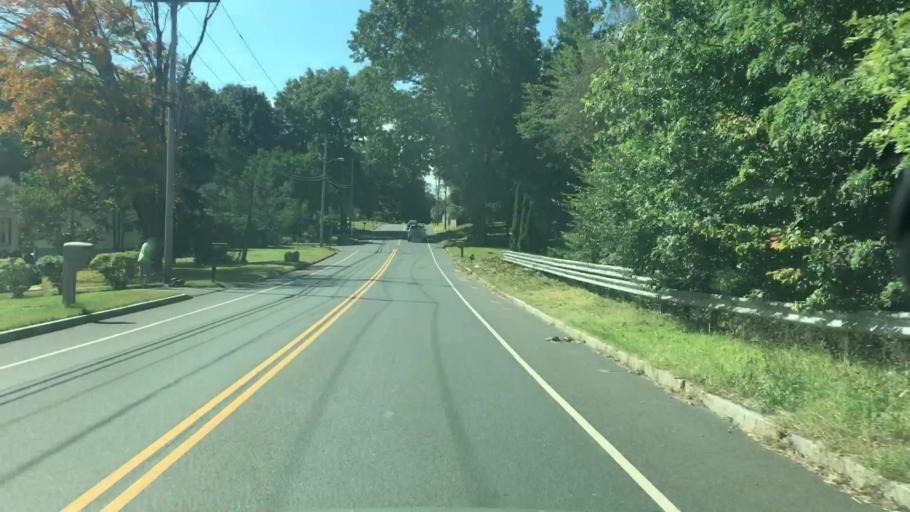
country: US
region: Connecticut
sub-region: Hartford County
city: Manchester
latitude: 41.7990
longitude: -72.5395
